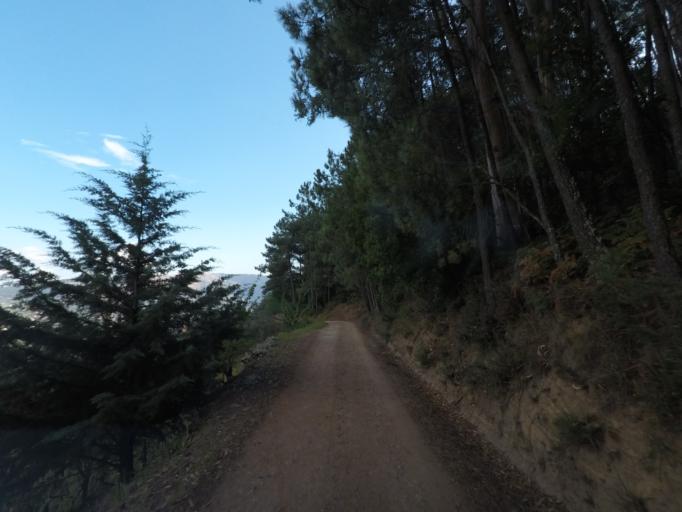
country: PT
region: Vila Real
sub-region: Mesao Frio
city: Mesao Frio
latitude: 41.1677
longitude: -7.9044
